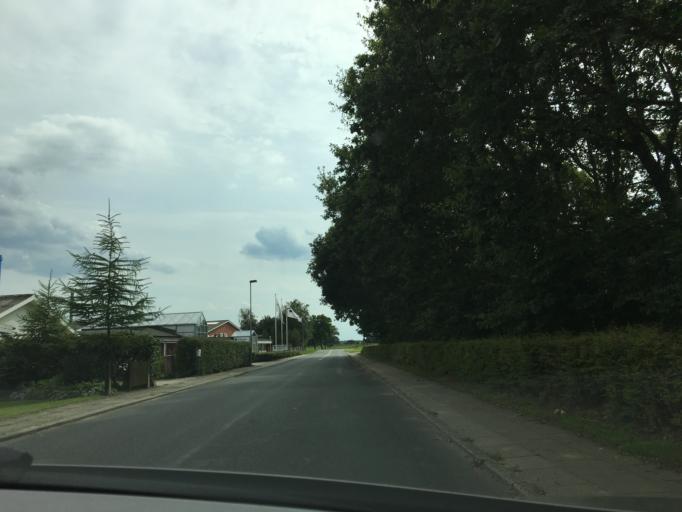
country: DK
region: Central Jutland
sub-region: Viborg Kommune
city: Stoholm
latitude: 56.4792
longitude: 9.1495
